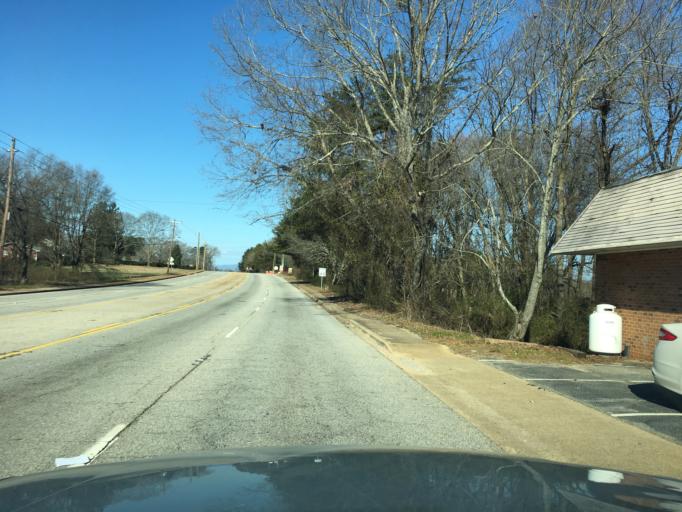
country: US
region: South Carolina
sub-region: Greenville County
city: Berea
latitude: 34.8865
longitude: -82.4610
